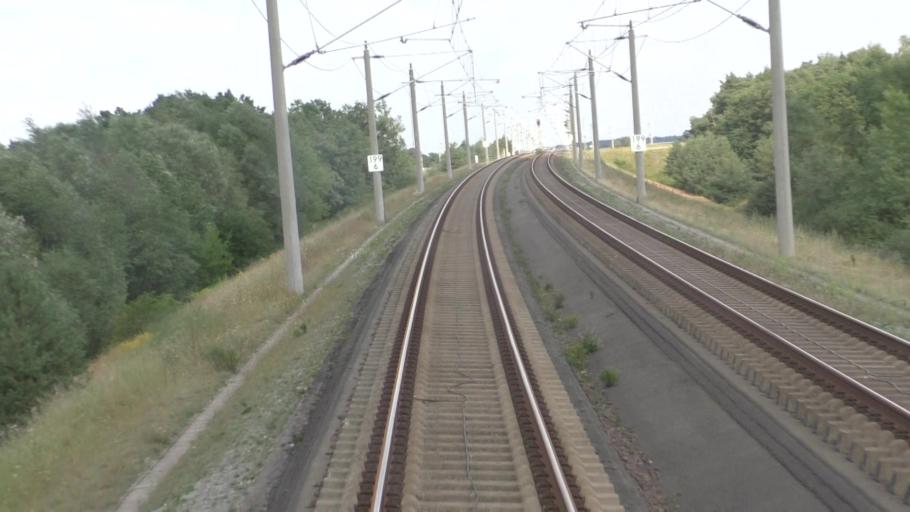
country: DE
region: Saxony-Anhalt
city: Hassel
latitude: 52.5941
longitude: 11.9344
